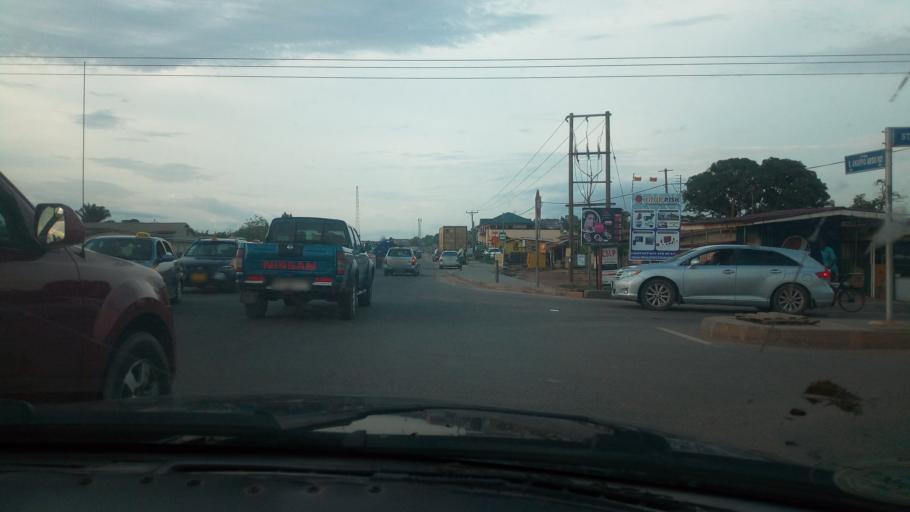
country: GH
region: Western
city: Takoradi
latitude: 4.9294
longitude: -1.7809
